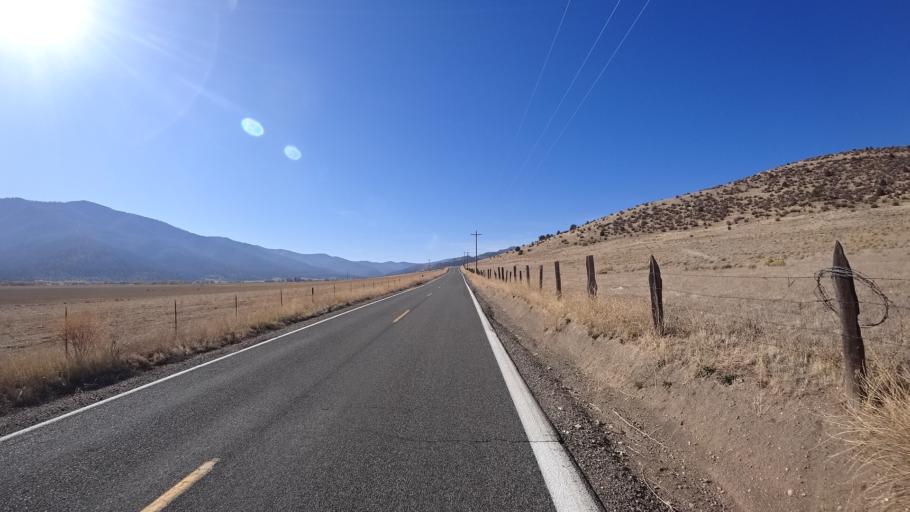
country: US
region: California
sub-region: Siskiyou County
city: Weed
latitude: 41.5098
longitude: -122.5303
